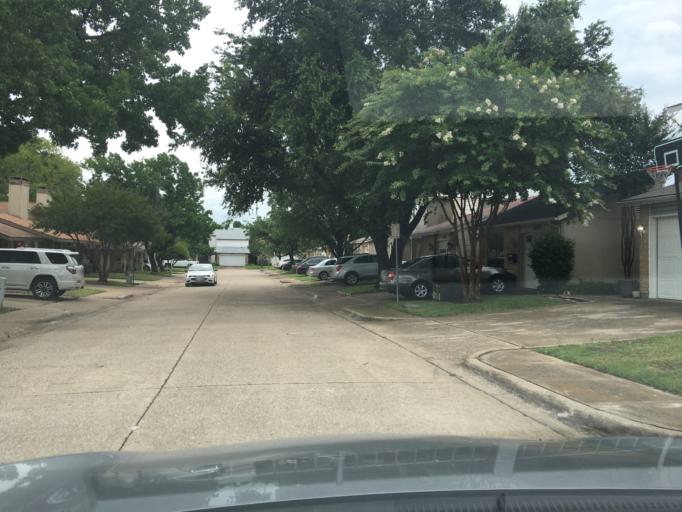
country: US
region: Texas
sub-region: Dallas County
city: Garland
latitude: 32.9506
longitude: -96.6712
